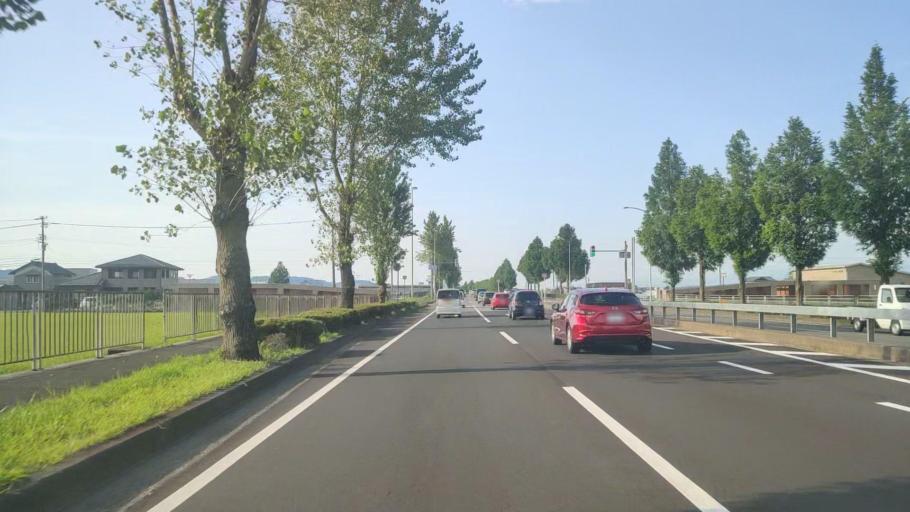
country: JP
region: Fukui
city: Sabae
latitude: 36.0023
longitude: 136.2076
